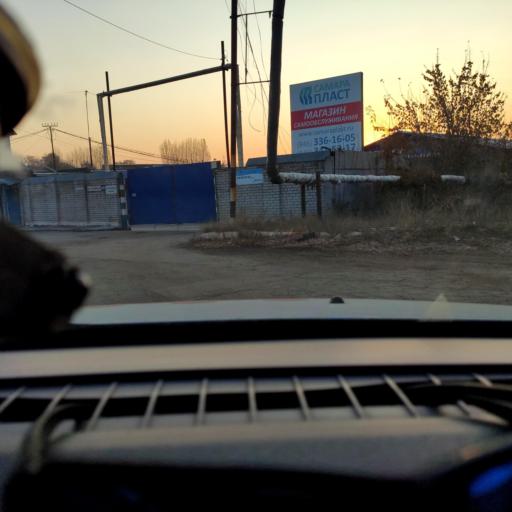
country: RU
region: Samara
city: Samara
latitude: 53.1804
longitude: 50.1459
